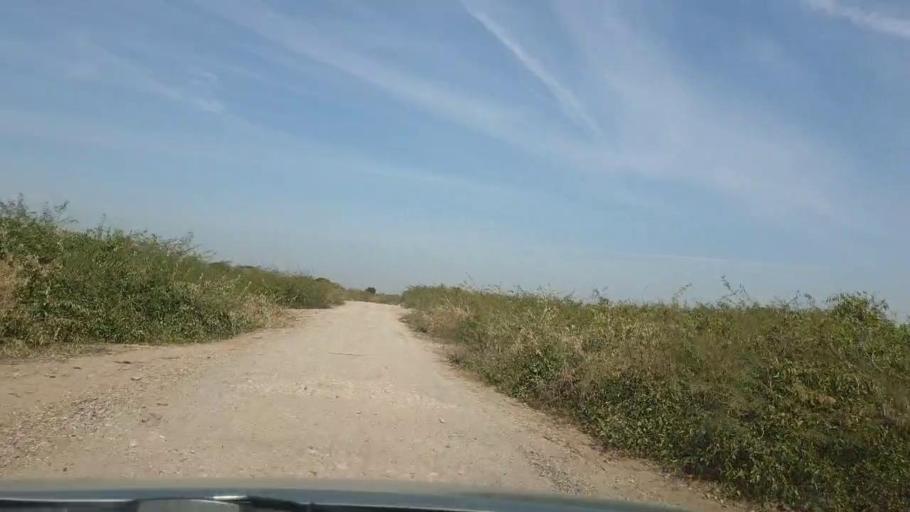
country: PK
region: Sindh
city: Nabisar
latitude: 25.1191
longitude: 69.6378
